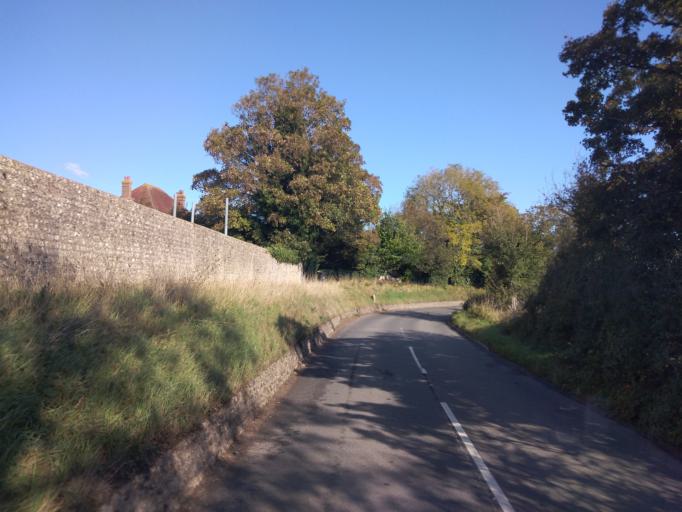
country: GB
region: England
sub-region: East Sussex
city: Seaford
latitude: 50.8107
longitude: 0.1590
